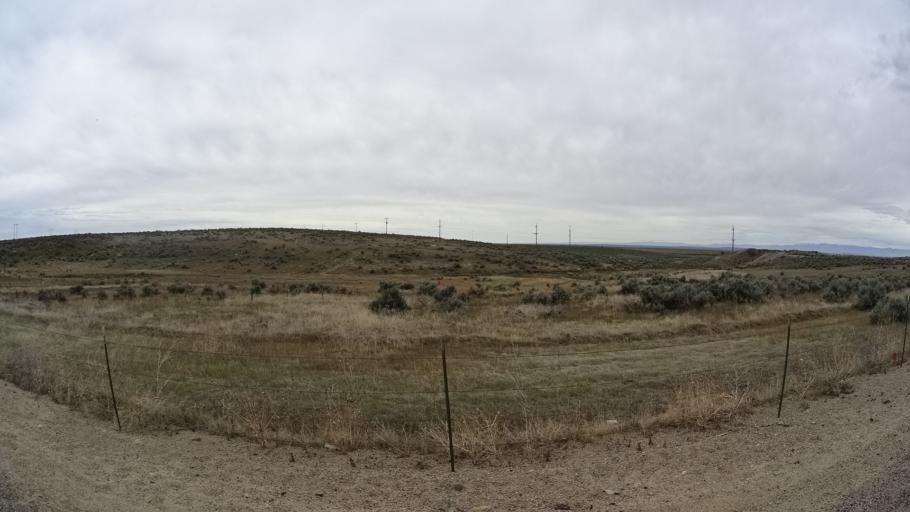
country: US
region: Idaho
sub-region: Ada County
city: Boise
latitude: 43.4683
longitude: -116.0811
